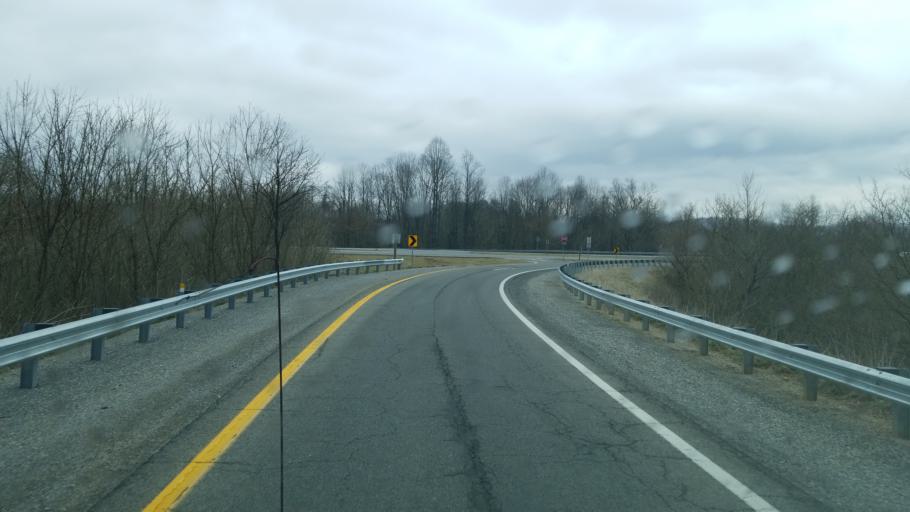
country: US
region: Virginia
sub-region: Giles County
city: Pearisburg
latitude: 37.3350
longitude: -80.7392
